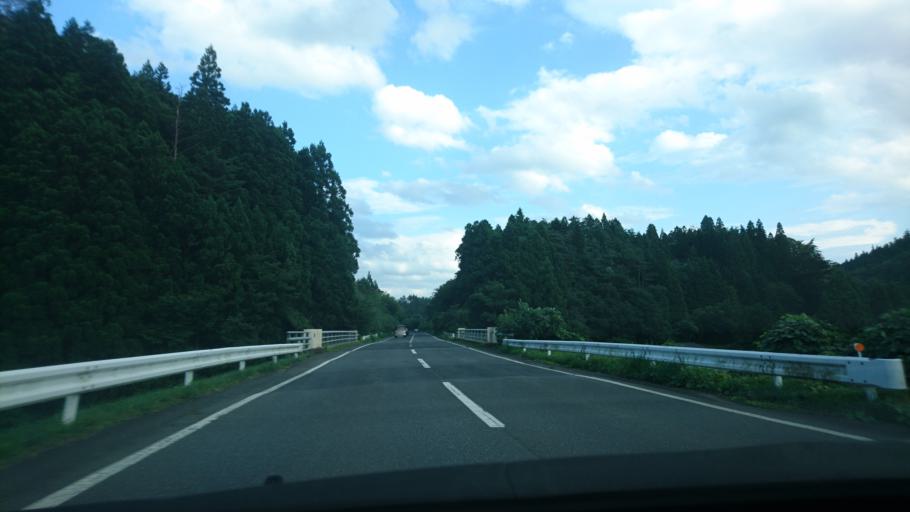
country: JP
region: Iwate
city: Mizusawa
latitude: 39.0392
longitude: 141.2471
